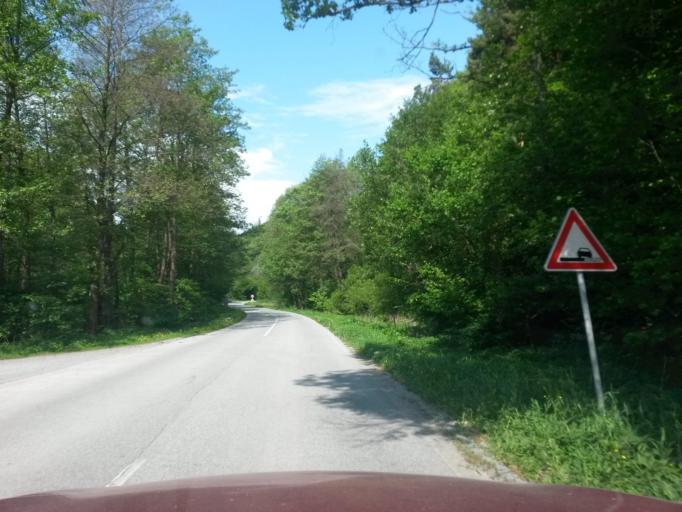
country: SK
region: Kosicky
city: Moldava nad Bodvou
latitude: 48.7255
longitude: 21.0794
